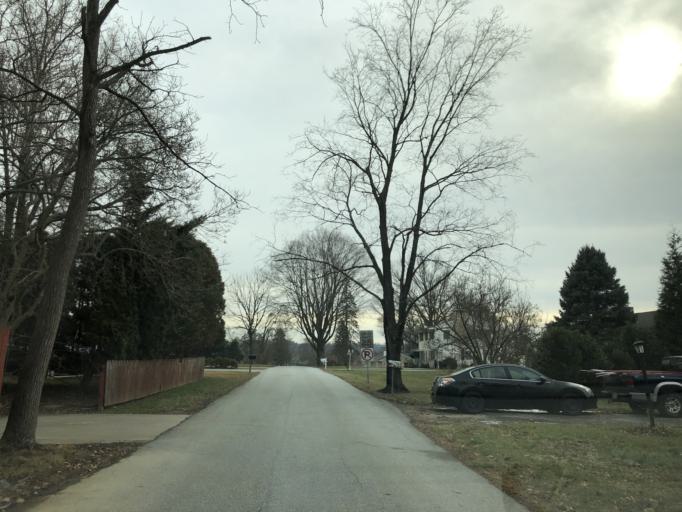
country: US
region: Pennsylvania
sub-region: Chester County
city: Exton
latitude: 40.0371
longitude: -75.6272
